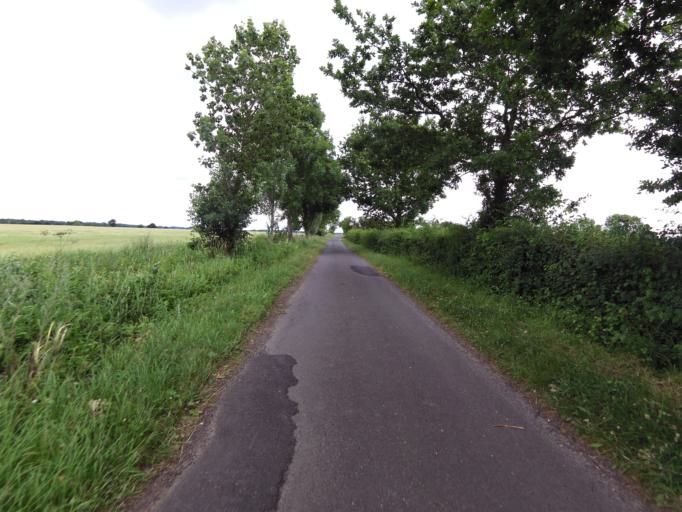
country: GB
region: England
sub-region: Norfolk
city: Harleston
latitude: 52.4036
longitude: 1.3236
